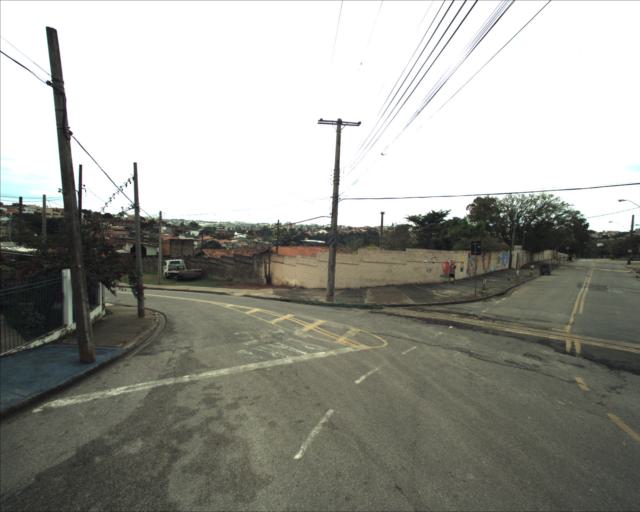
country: BR
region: Sao Paulo
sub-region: Sorocaba
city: Sorocaba
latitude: -23.5045
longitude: -47.5032
